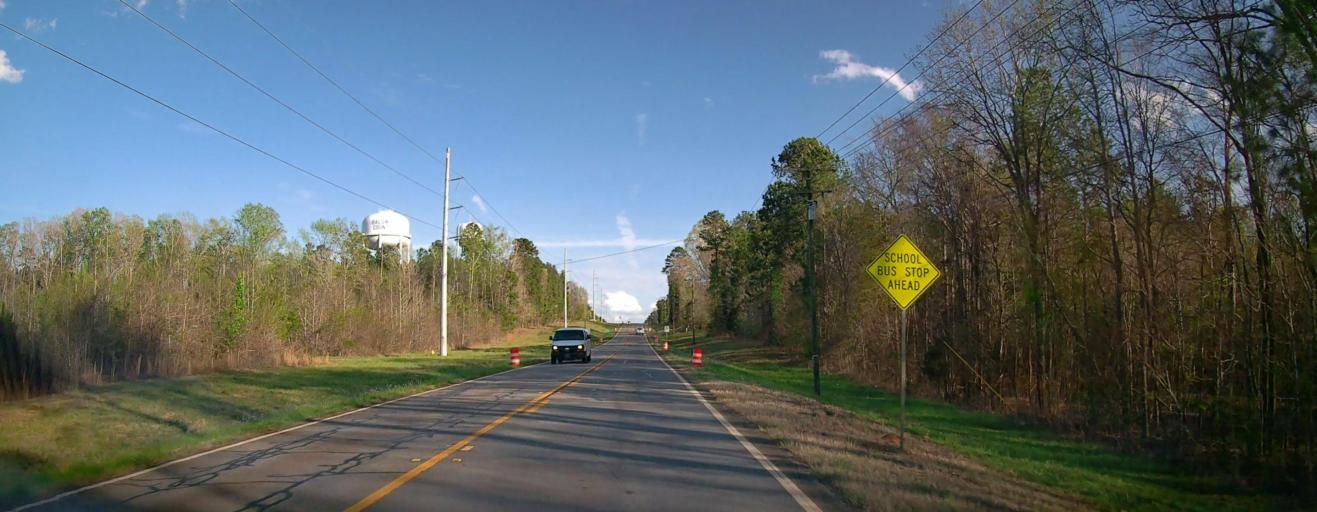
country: US
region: Georgia
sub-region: Baldwin County
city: Milledgeville
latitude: 33.1431
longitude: -83.3344
